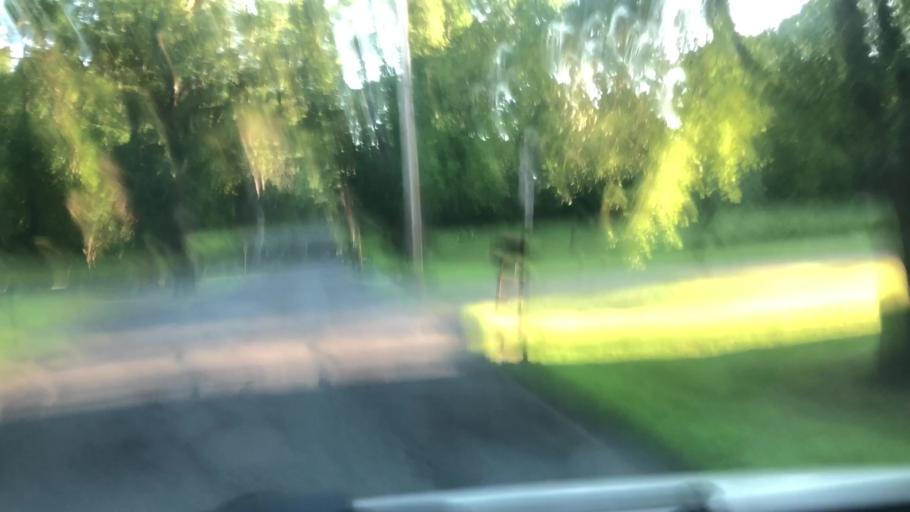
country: US
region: Massachusetts
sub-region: Hampshire County
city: Easthampton
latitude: 42.2920
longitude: -72.7165
